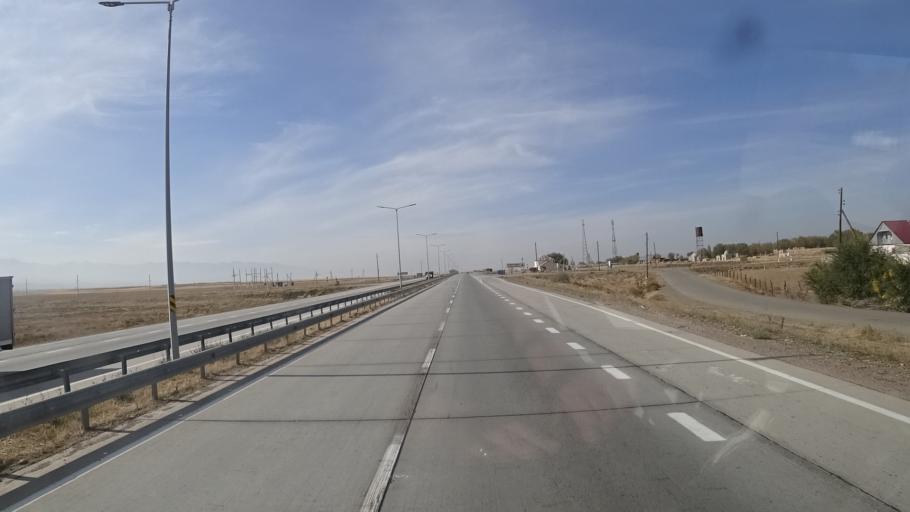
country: KZ
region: Zhambyl
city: Merke
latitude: 42.8890
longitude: 72.9898
